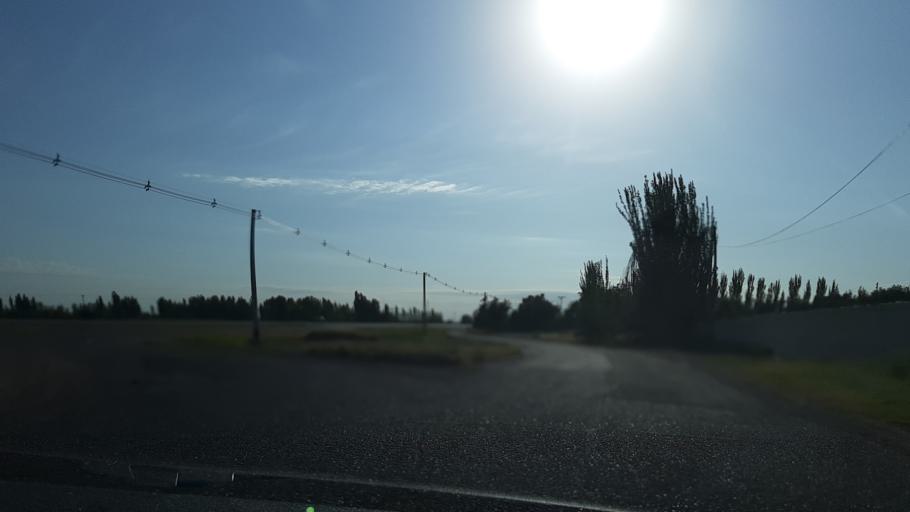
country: AR
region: Mendoza
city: San Martin
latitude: -33.0416
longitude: -68.5197
